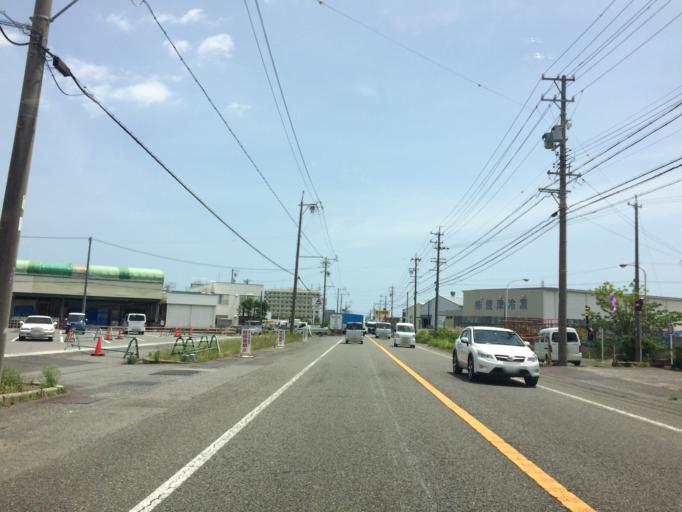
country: JP
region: Shizuoka
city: Yaizu
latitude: 34.8870
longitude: 138.2926
